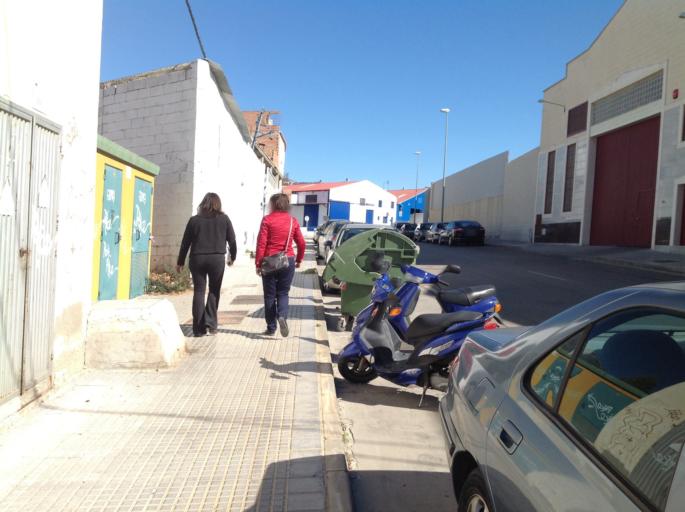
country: ES
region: Andalusia
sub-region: Provincia de Malaga
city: Velez-Malaga
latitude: 36.7653
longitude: -4.0933
